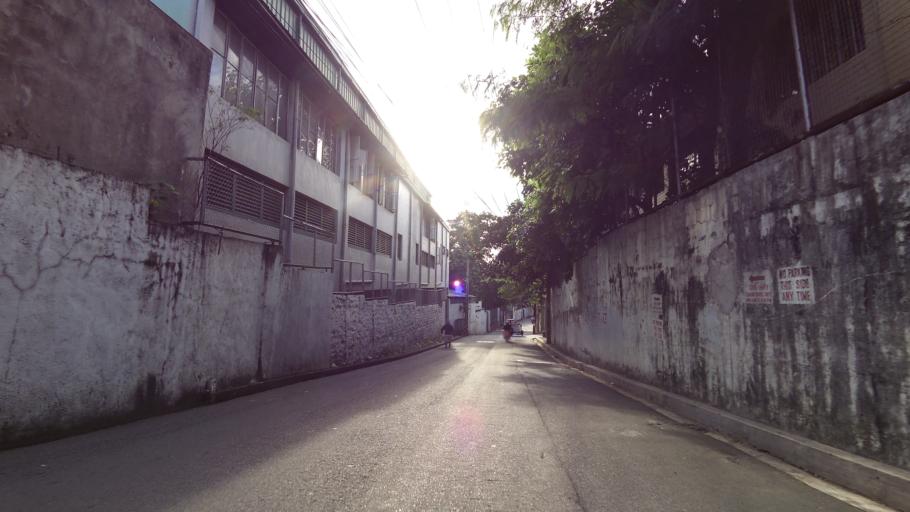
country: PH
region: Metro Manila
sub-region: San Juan
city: San Juan
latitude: 14.6032
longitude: 121.0298
